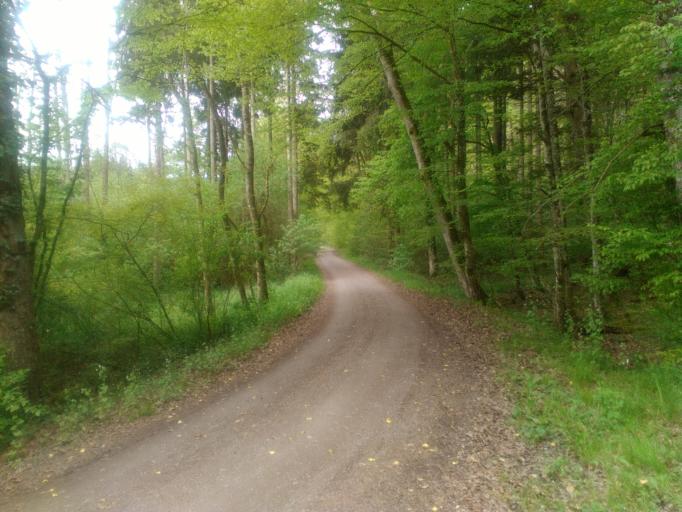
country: DE
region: Baden-Wuerttemberg
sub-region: Regierungsbezirk Stuttgart
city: Schlaitdorf
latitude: 48.6068
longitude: 9.1846
